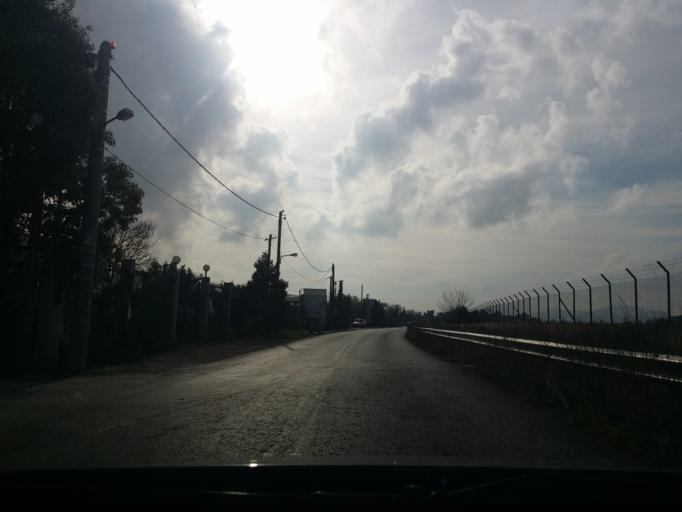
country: GR
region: Attica
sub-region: Nomarchia Anatolikis Attikis
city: Varybobi
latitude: 38.1057
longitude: 23.7881
